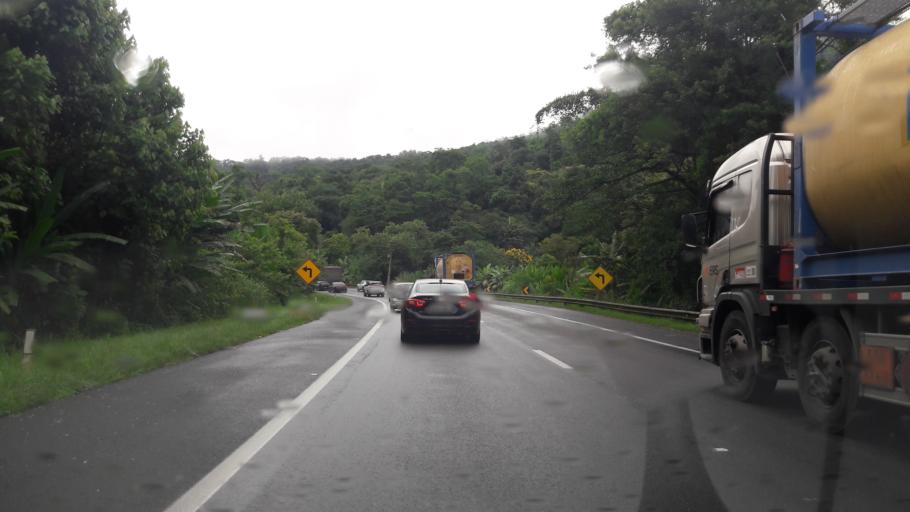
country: BR
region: Parana
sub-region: Antonina
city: Antonina
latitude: -25.5610
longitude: -48.8160
